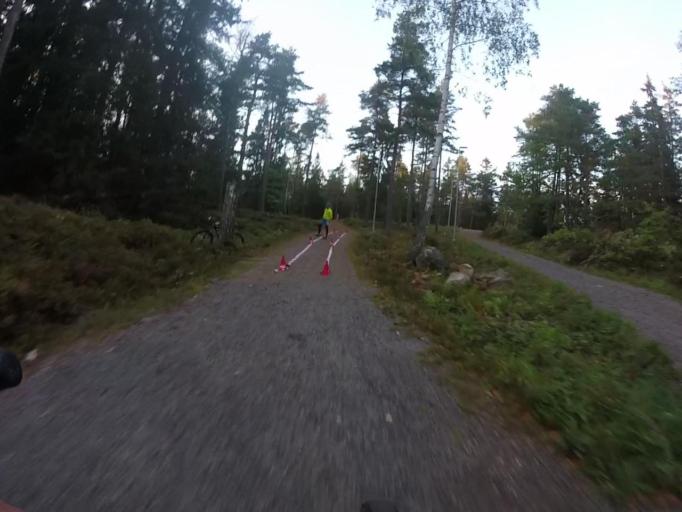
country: SE
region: Vaestra Goetaland
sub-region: Trollhattan
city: Trollhattan
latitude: 58.2964
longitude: 12.2695
